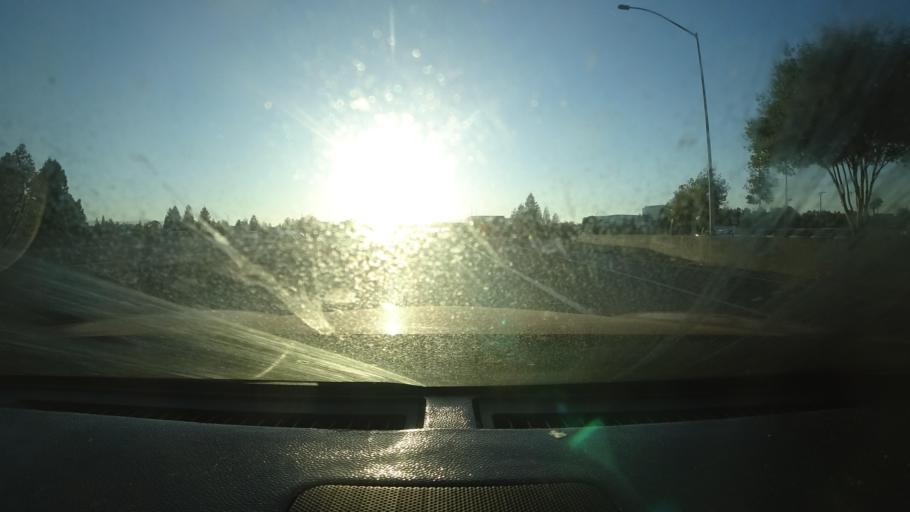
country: US
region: California
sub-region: Santa Clara County
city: Santa Clara
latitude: 37.3816
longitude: -121.9613
